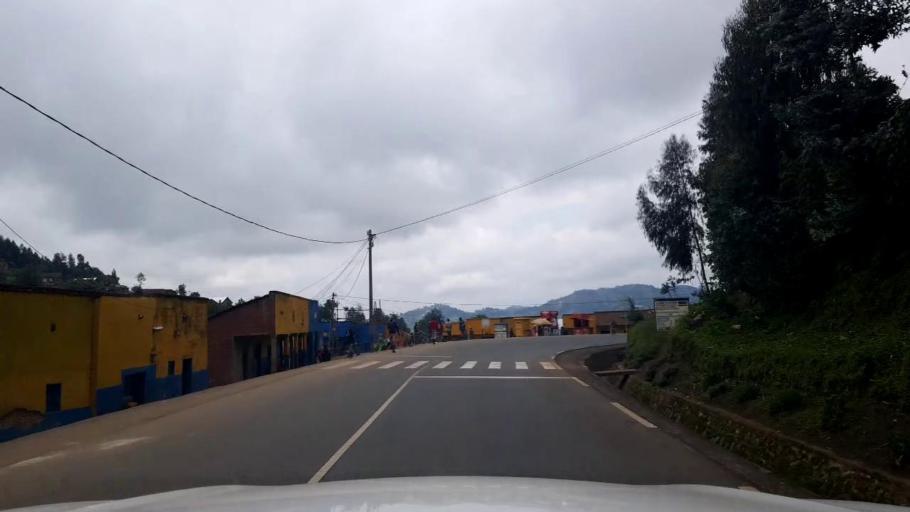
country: RW
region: Northern Province
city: Musanze
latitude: -1.6460
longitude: 29.5057
